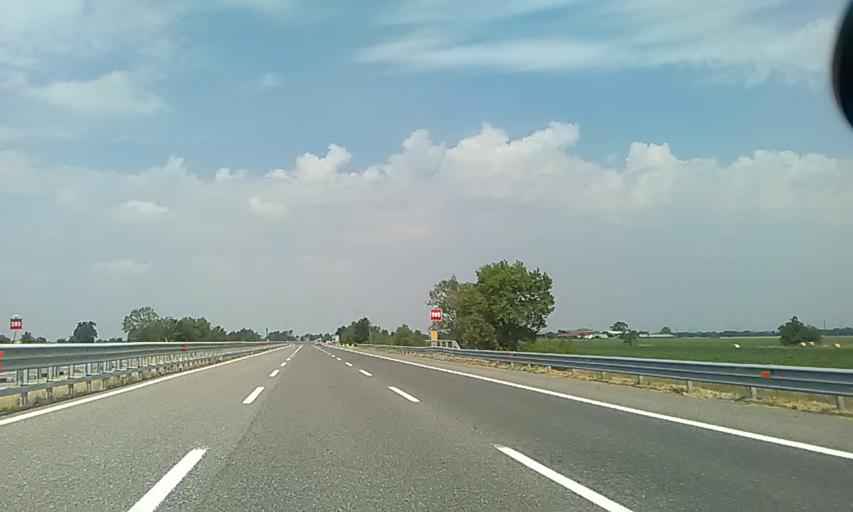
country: IT
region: Piedmont
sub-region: Provincia di Alessandria
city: Castelspina
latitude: 44.8054
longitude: 8.6023
